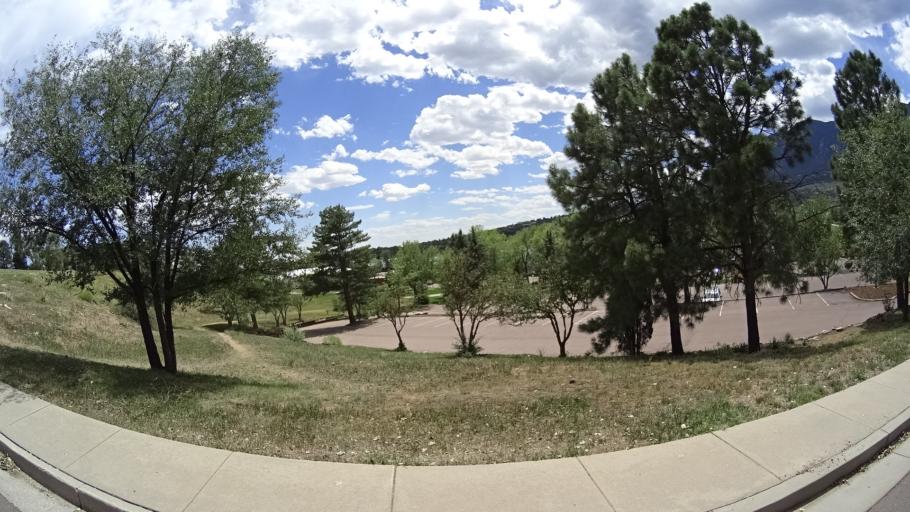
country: US
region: Colorado
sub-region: El Paso County
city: Stratmoor
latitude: 38.7839
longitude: -104.8234
